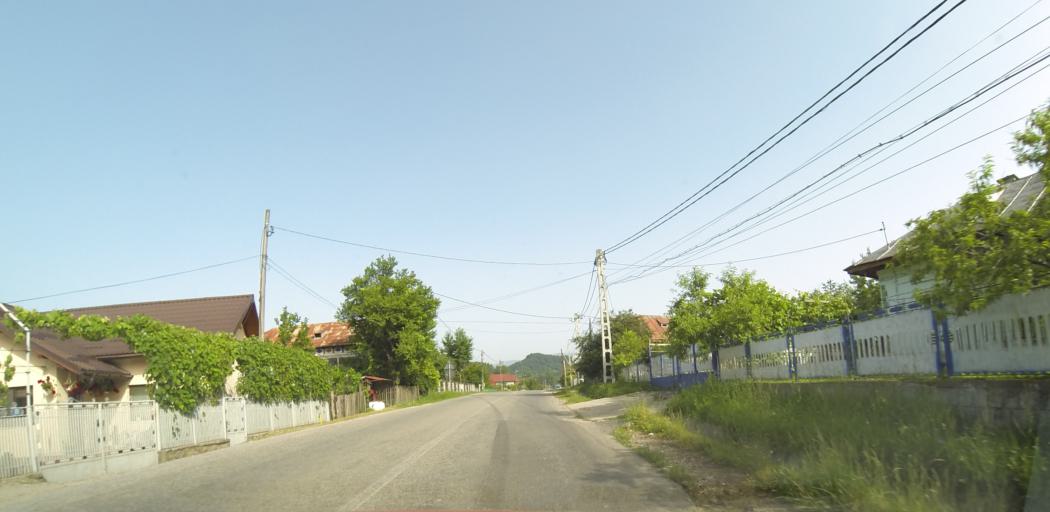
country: RO
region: Valcea
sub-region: Comuna Pausesti-Maglasi
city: Pausesti-Maglasi
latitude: 45.1326
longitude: 24.2573
